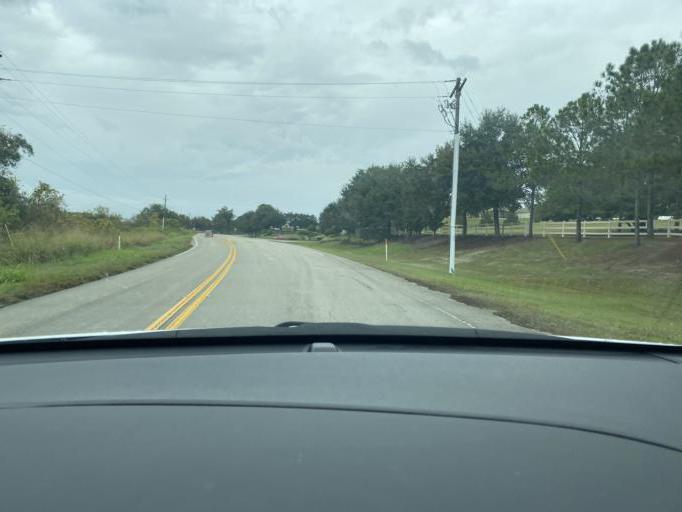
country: US
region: Florida
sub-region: Lake County
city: Clermont
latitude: 28.5969
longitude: -81.7939
